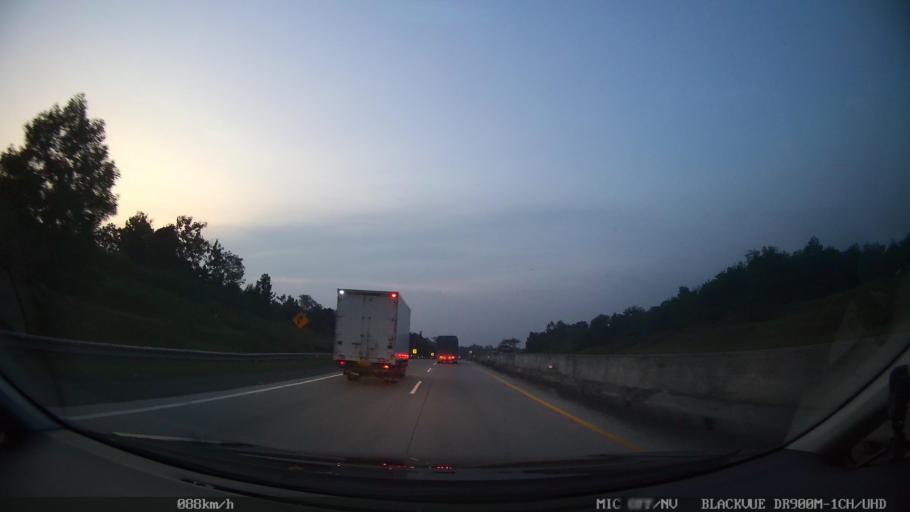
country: ID
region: Lampung
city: Sidorejo
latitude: -5.5592
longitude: 105.5292
